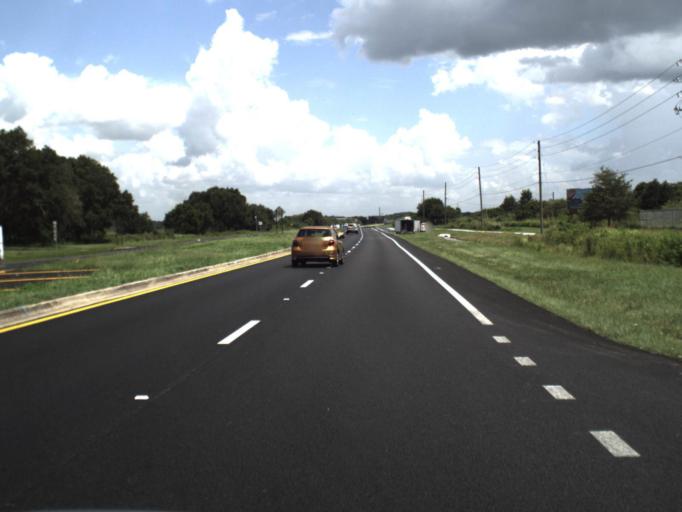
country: US
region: Florida
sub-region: Polk County
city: Cypress Gardens
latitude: 27.9785
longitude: -81.6455
